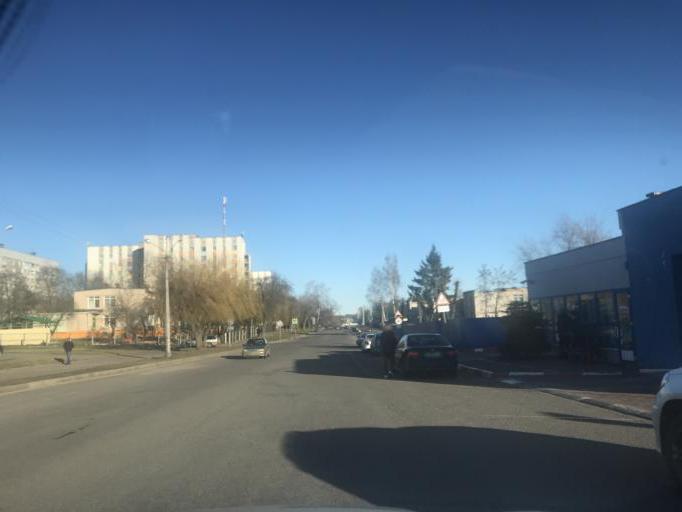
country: BY
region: Mogilev
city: Mahilyow
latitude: 53.9112
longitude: 30.3489
